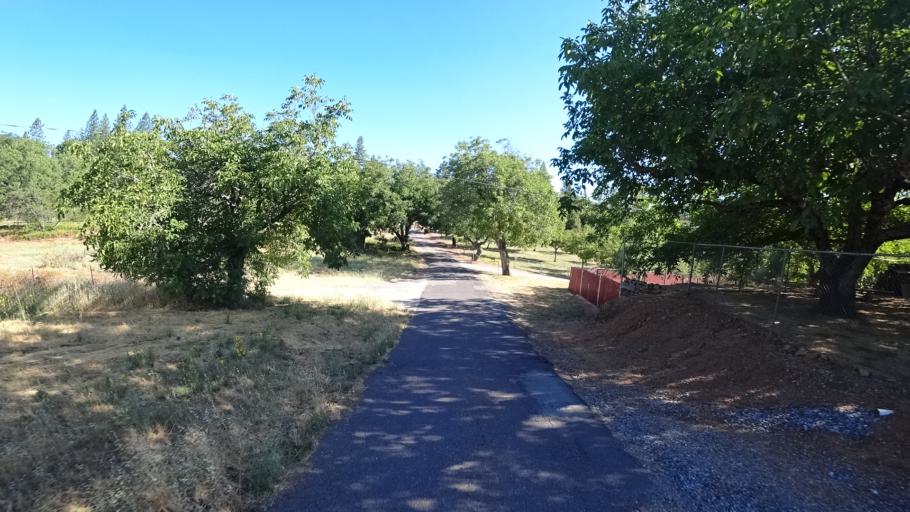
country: US
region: California
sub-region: Amador County
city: Pioneer
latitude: 38.4115
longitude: -120.5503
